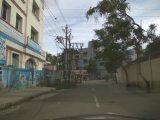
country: IN
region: Karnataka
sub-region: Bangalore Urban
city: Bangalore
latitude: 12.9824
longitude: 77.5386
